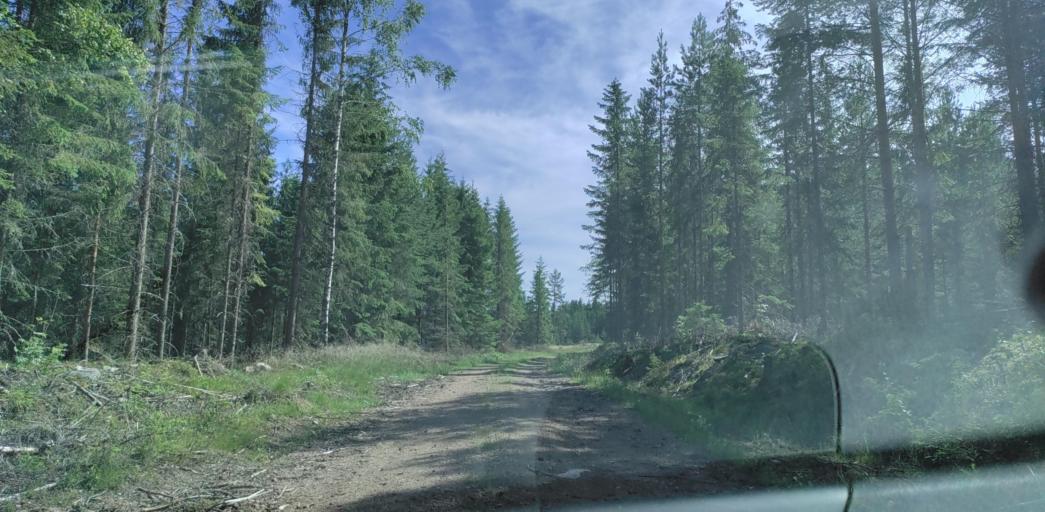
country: SE
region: Vaermland
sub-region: Hagfors Kommun
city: Ekshaerad
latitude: 60.0963
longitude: 13.3729
